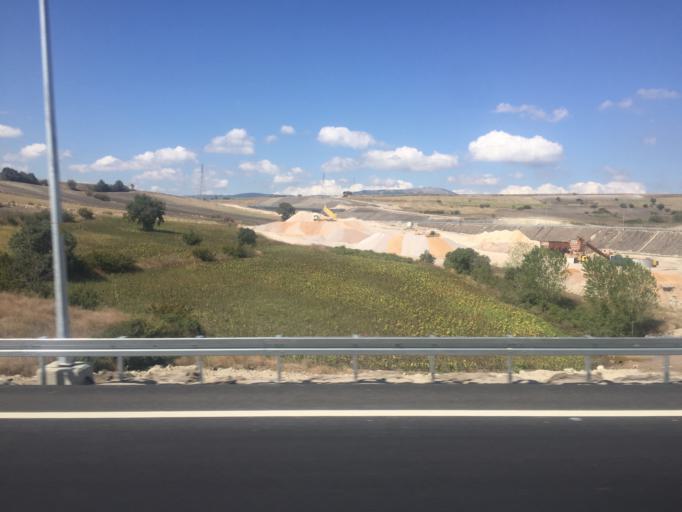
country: TR
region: Balikesir
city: Susurluk
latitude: 39.9668
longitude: 28.1635
